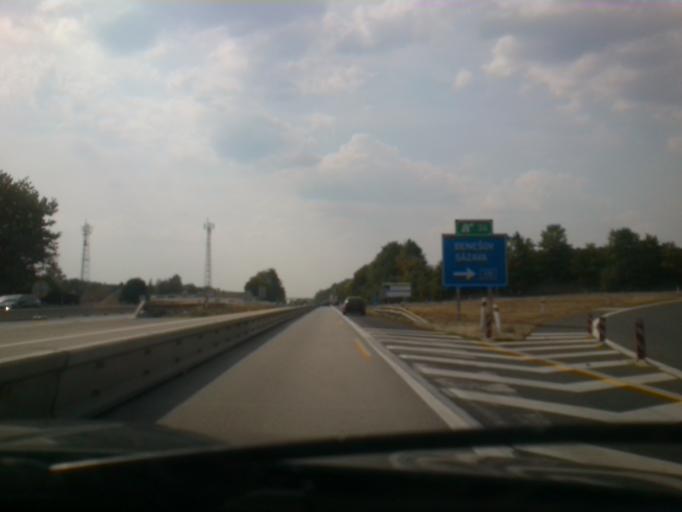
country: CZ
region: Central Bohemia
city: Divisov
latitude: 49.8384
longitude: 14.8314
